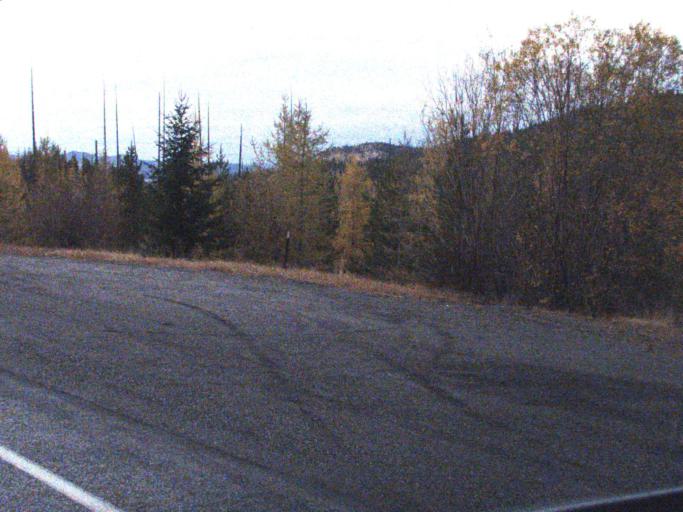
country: US
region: Washington
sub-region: Ferry County
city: Republic
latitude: 48.6002
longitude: -118.5331
